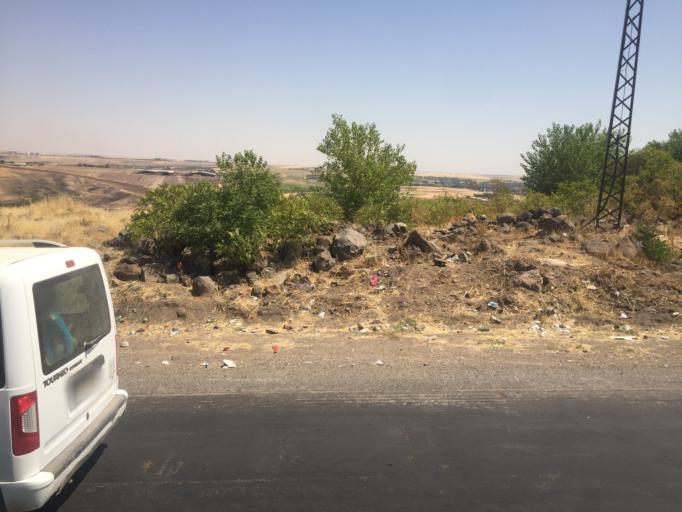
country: TR
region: Diyarbakir
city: Diyarbakir
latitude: 37.8738
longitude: 40.2211
